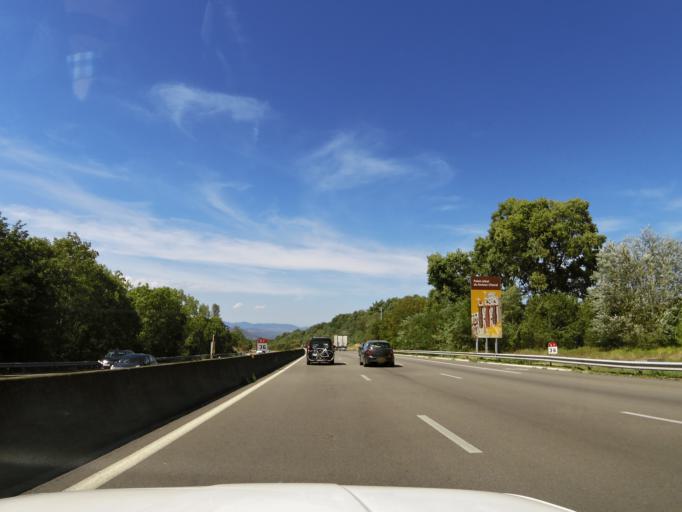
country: FR
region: Rhone-Alpes
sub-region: Departement de la Drome
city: Beausemblant
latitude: 45.2227
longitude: 4.8581
